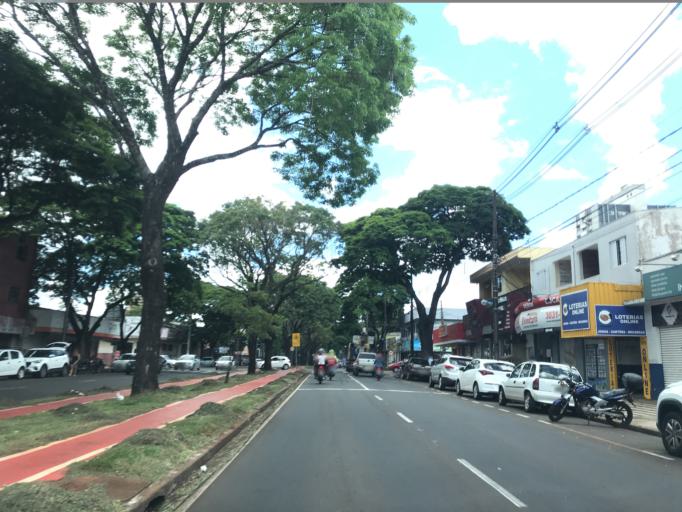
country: BR
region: Parana
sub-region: Maringa
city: Maringa
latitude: -23.4115
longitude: -51.9246
